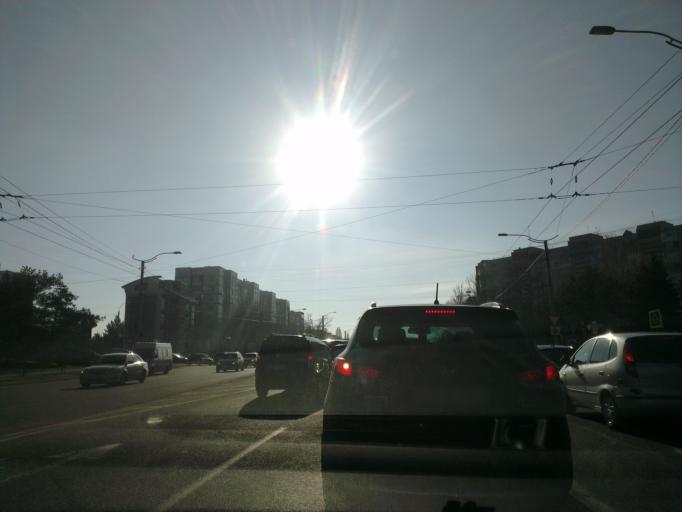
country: MD
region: Chisinau
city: Chisinau
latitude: 47.0397
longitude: 28.8814
